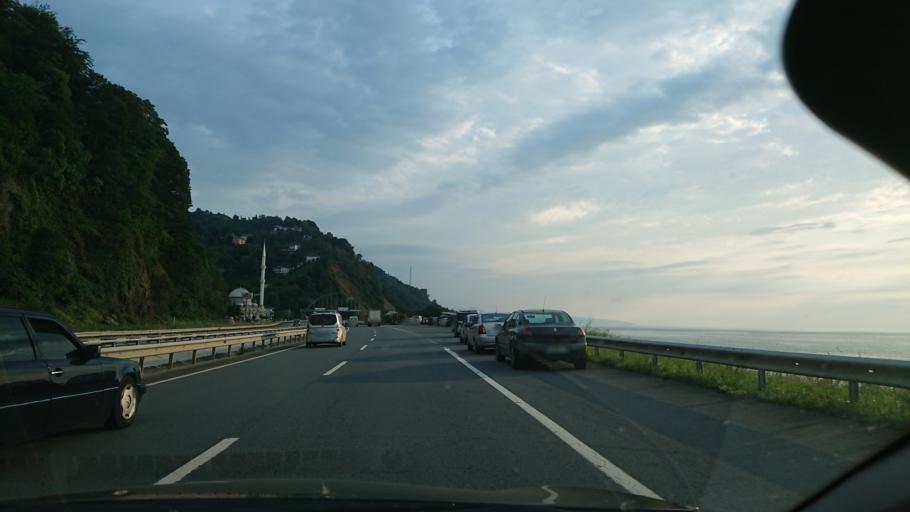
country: TR
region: Rize
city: Pazar
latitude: 41.1588
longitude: 40.7988
